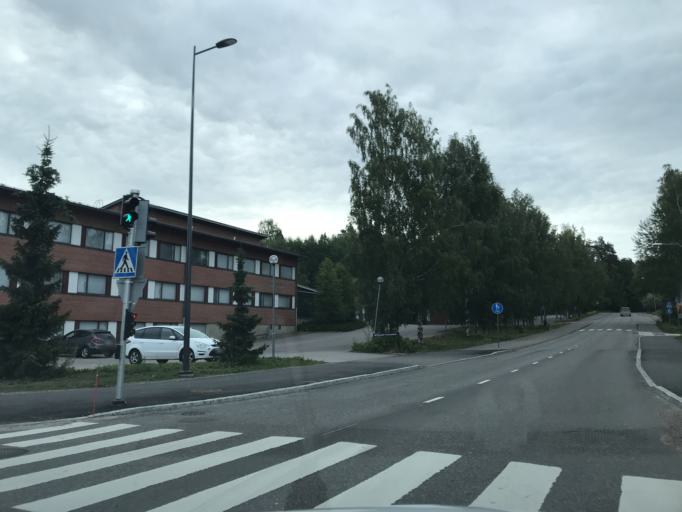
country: FI
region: Uusimaa
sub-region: Helsinki
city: Nurmijaervi
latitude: 60.3801
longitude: 24.7454
